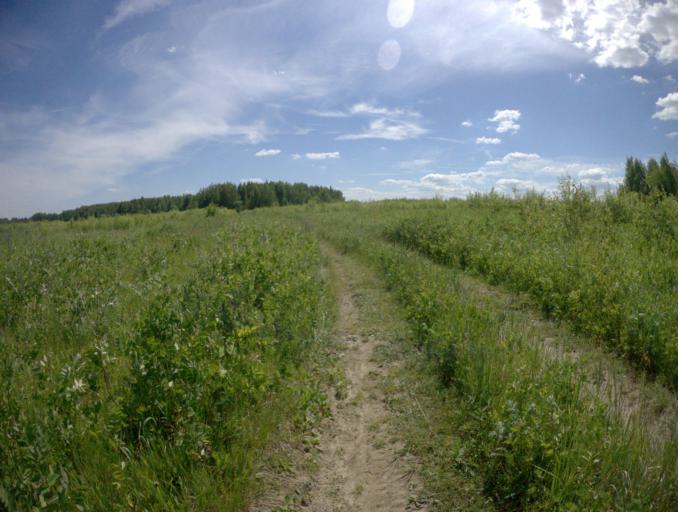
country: RU
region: Vladimir
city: Stavrovo
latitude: 56.3366
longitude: 40.0693
